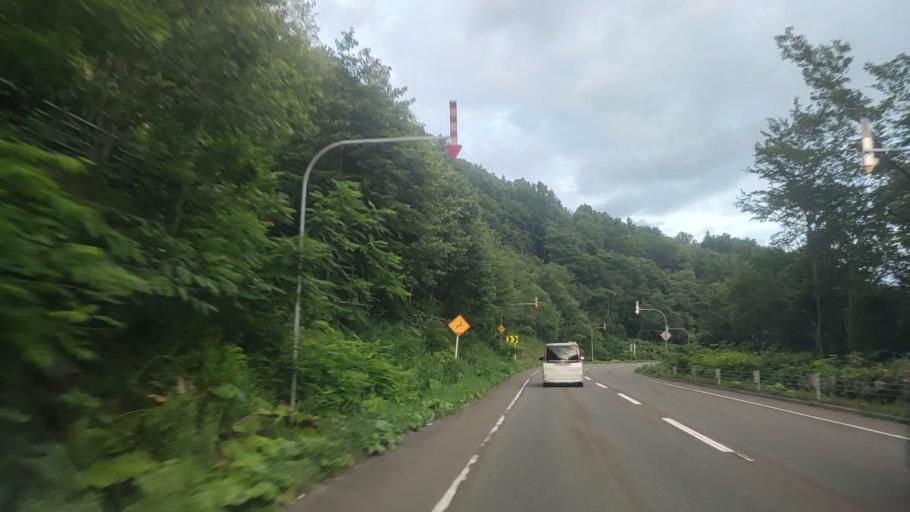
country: JP
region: Hokkaido
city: Shimo-furano
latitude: 43.3613
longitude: 142.2419
